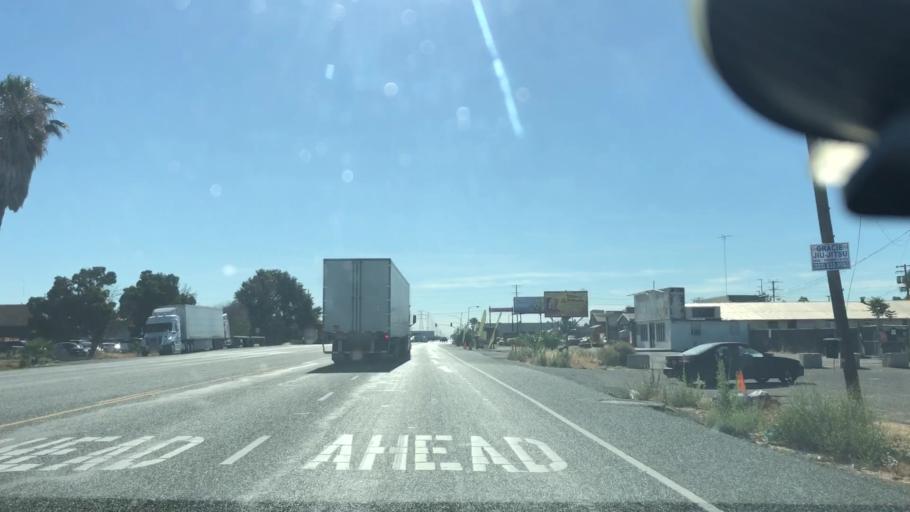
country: US
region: California
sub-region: San Joaquin County
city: Tracy
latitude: 37.7397
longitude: -121.4017
